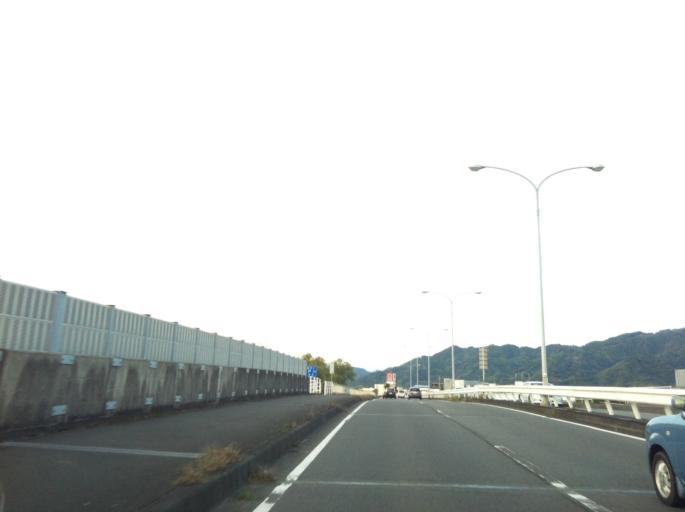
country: JP
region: Shizuoka
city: Yaizu
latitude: 34.8708
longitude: 138.2993
